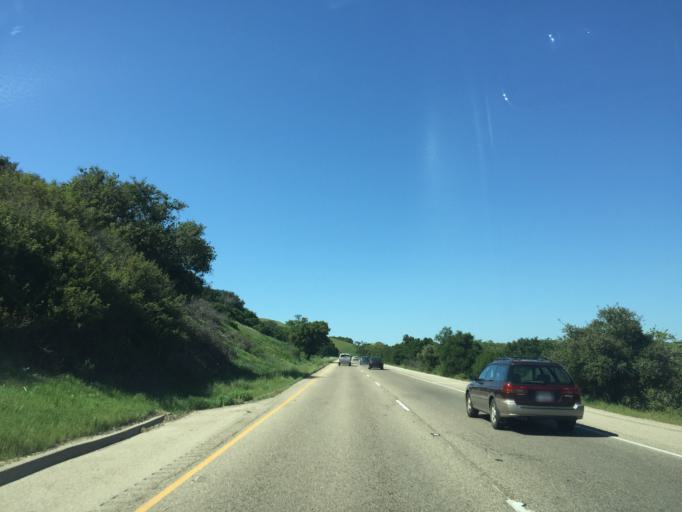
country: US
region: California
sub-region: Santa Barbara County
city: Los Olivos
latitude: 34.6986
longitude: -120.1645
